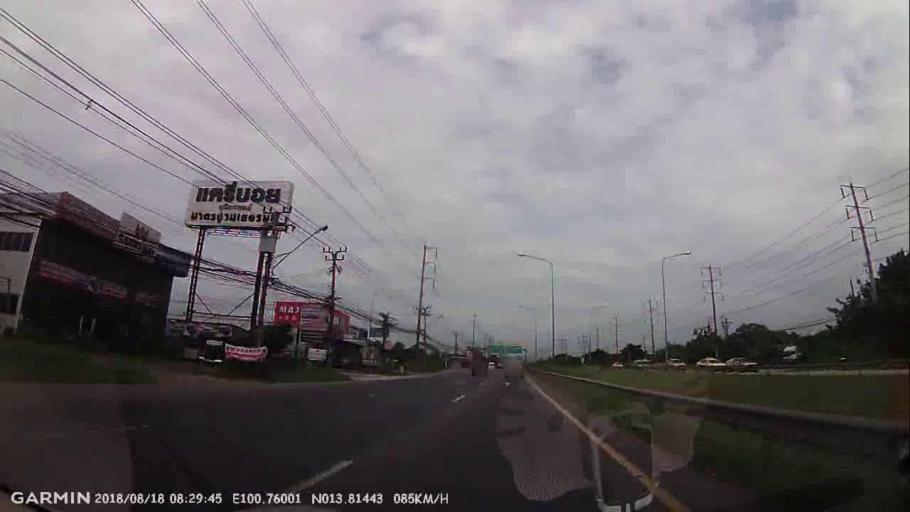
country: TH
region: Bangkok
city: Min Buri
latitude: 13.8139
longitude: 100.7603
